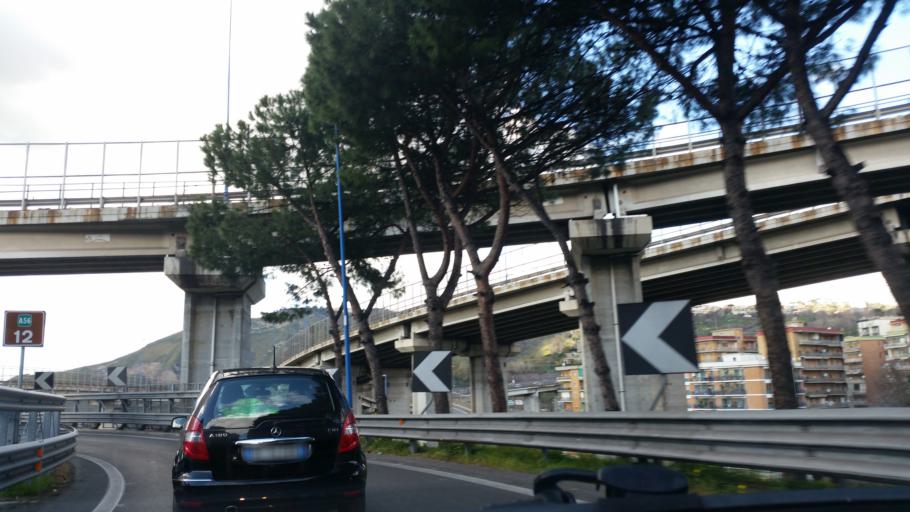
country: IT
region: Campania
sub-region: Provincia di Napoli
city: Napoli
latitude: 40.8456
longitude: 14.2187
